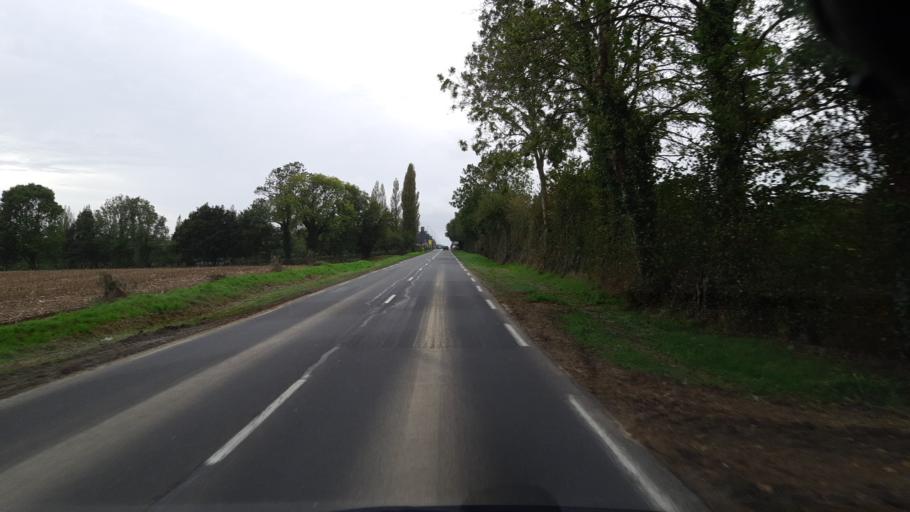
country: FR
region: Lower Normandy
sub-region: Departement de la Manche
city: Gavray
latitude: 48.9411
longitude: -1.3222
